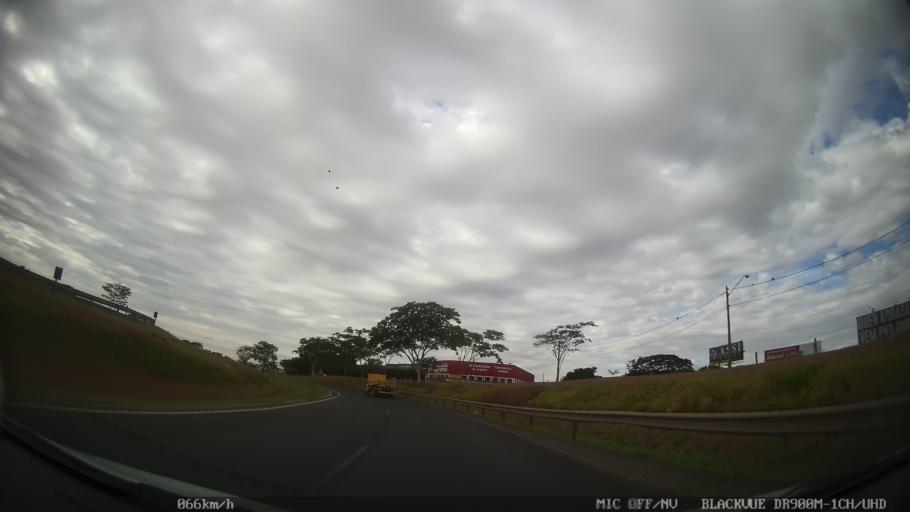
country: BR
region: Sao Paulo
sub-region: Bady Bassitt
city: Bady Bassitt
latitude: -20.8062
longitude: -49.5234
